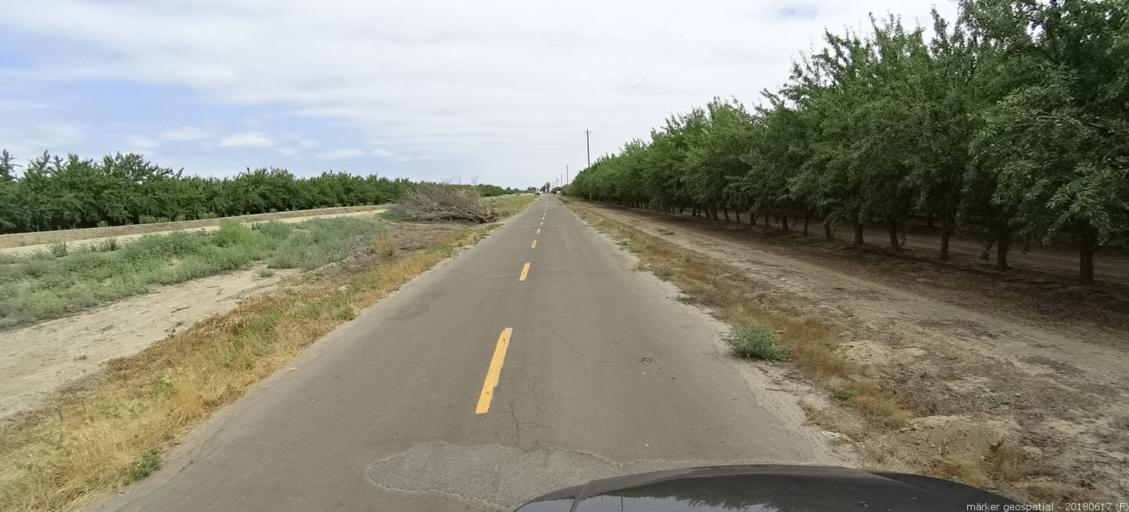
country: US
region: California
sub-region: Madera County
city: Fairmead
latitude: 37.0003
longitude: -120.2205
